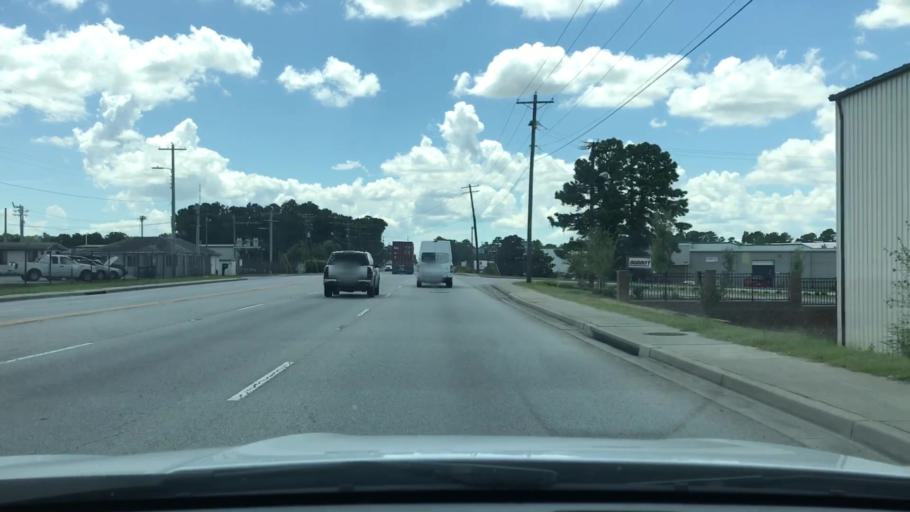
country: US
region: South Carolina
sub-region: Berkeley County
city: Hanahan
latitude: 32.9123
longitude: -79.9860
